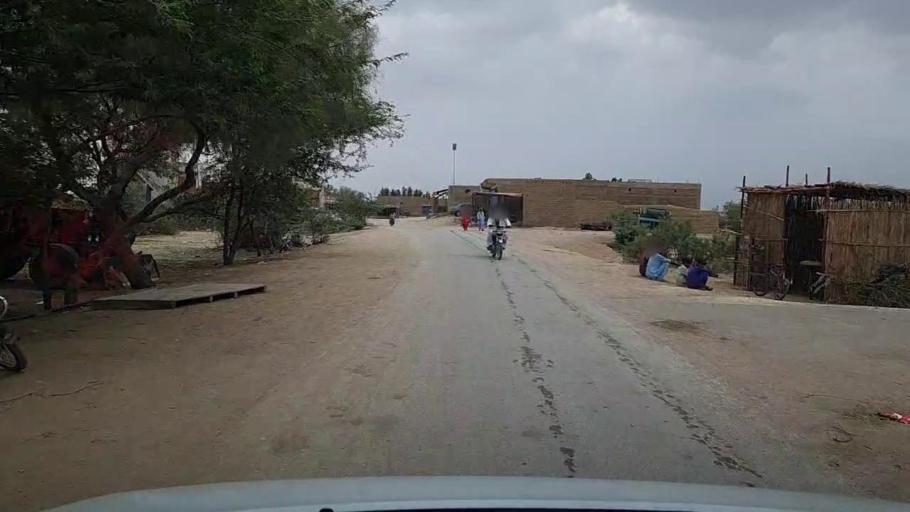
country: PK
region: Sindh
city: Sehwan
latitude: 26.3395
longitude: 67.7217
